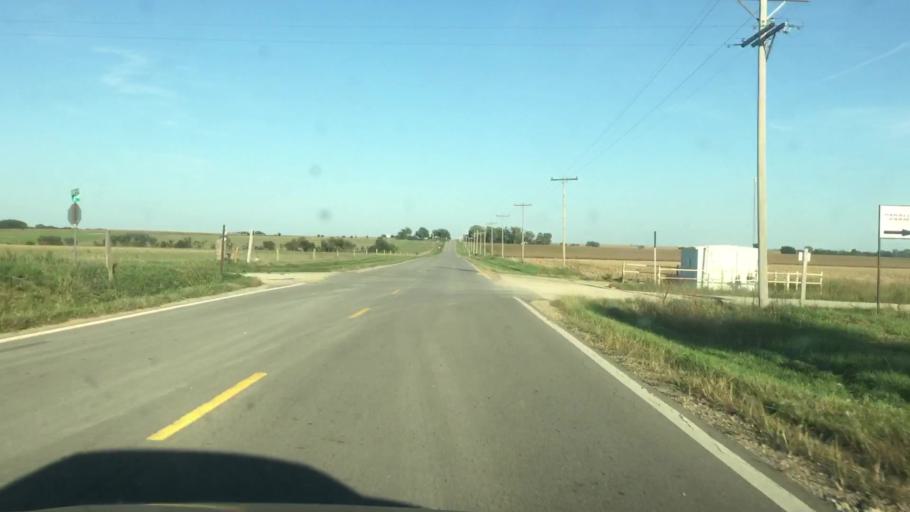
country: US
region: Kansas
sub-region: Brown County
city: Horton
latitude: 39.5876
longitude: -95.6021
